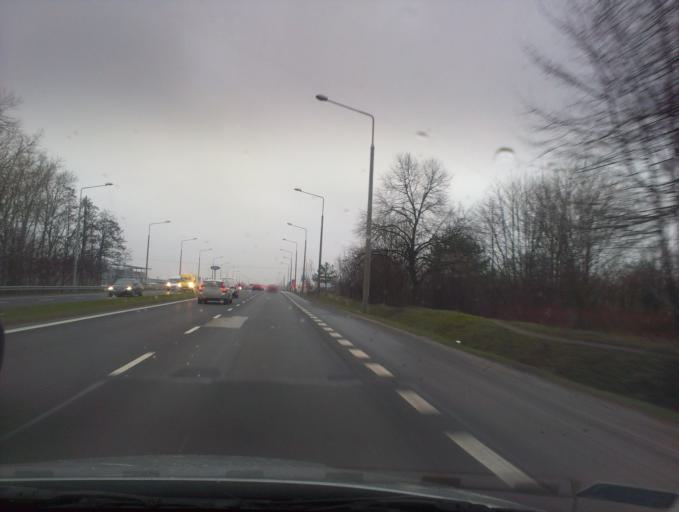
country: PL
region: Masovian Voivodeship
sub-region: Radom
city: Radom
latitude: 51.4569
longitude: 21.1411
